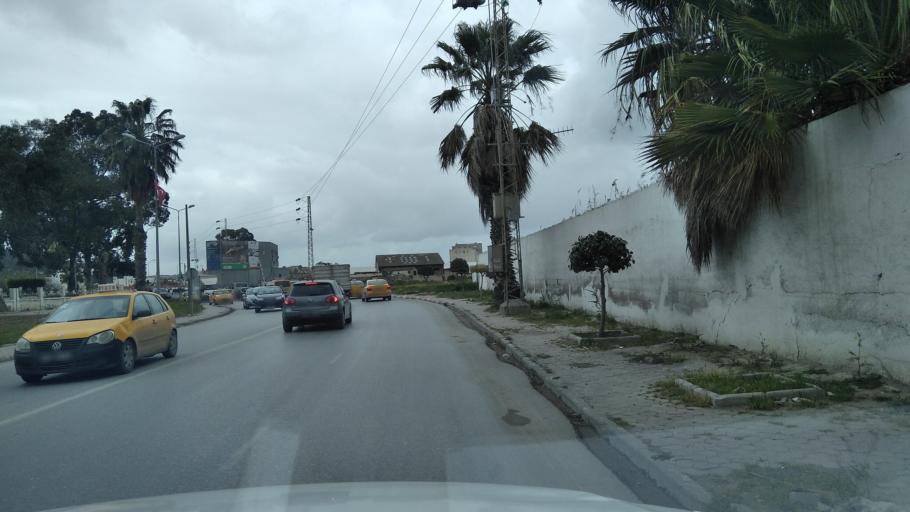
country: TN
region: Bin 'Arus
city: Ben Arous
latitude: 36.7590
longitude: 10.2172
